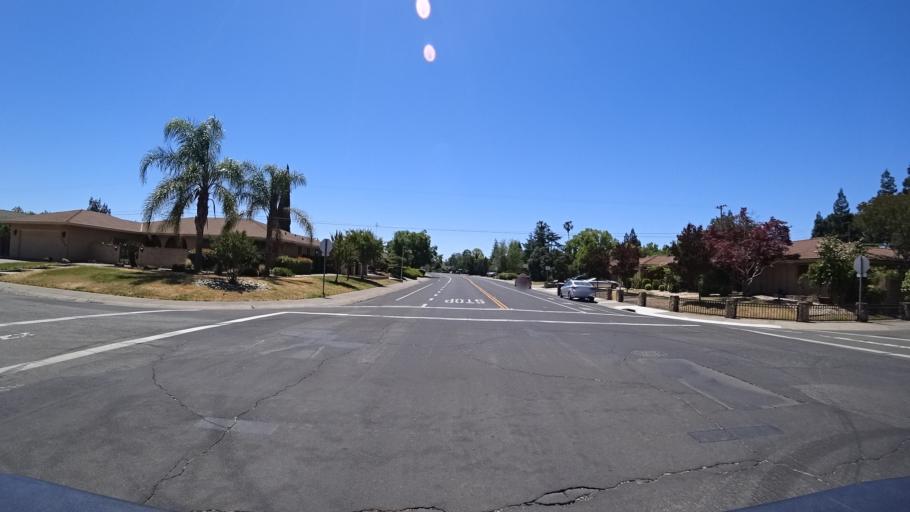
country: US
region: California
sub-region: Sacramento County
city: Parkway
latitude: 38.5014
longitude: -121.5161
